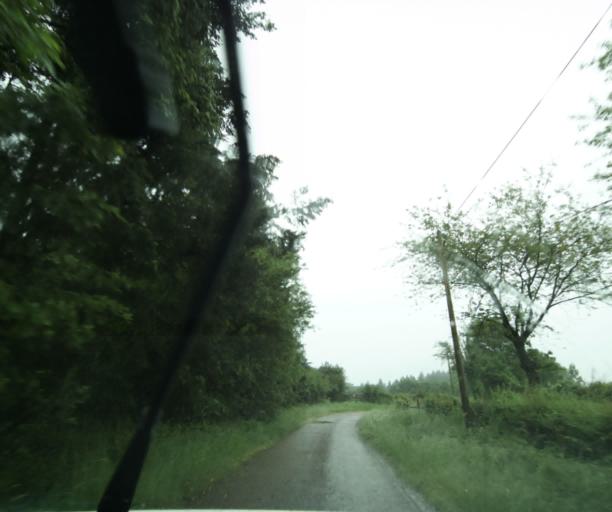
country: FR
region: Bourgogne
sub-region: Departement de Saone-et-Loire
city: Charolles
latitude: 46.3805
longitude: 4.3114
